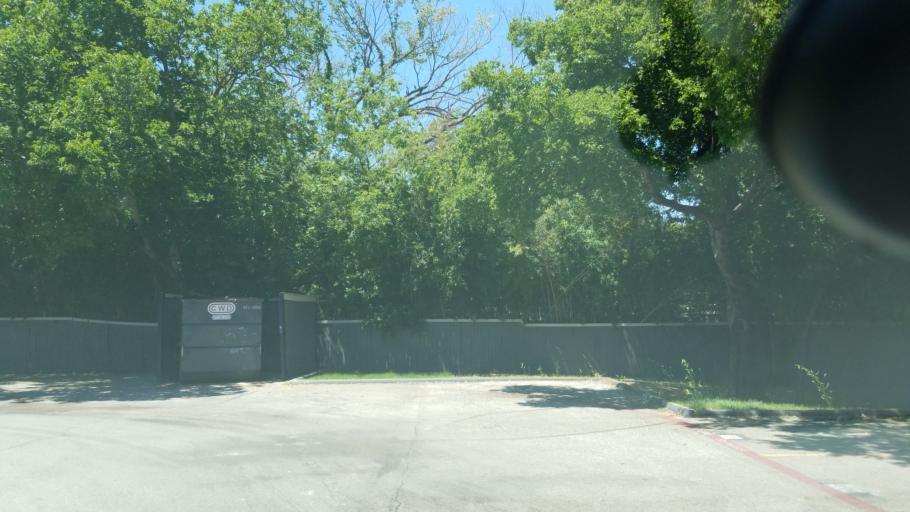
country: US
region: Texas
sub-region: Dallas County
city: Irving
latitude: 32.8282
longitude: -96.9338
